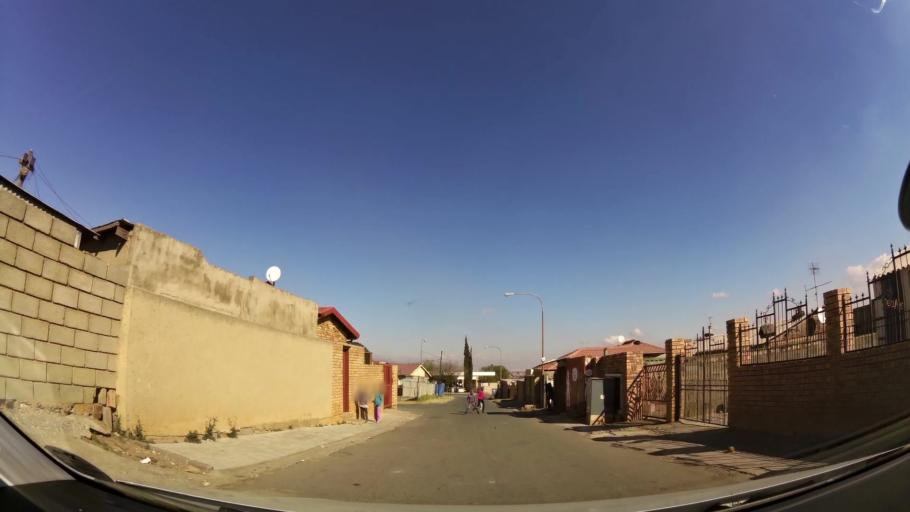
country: ZA
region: Gauteng
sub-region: City of Johannesburg Metropolitan Municipality
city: Roodepoort
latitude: -26.2134
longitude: 27.8873
